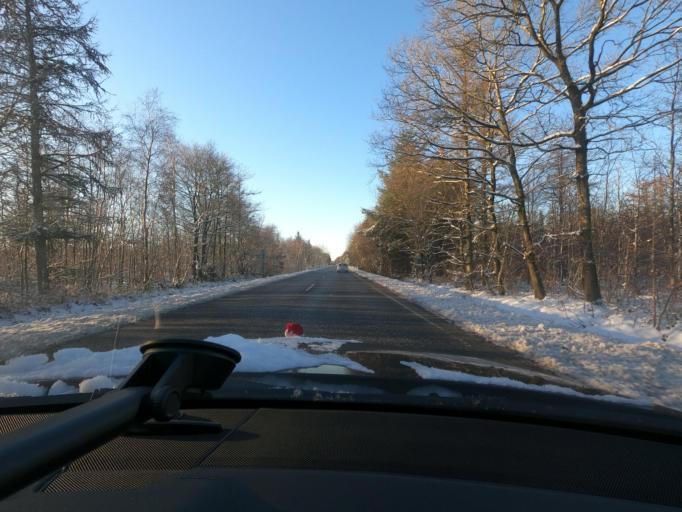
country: DK
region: South Denmark
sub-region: Tonder Kommune
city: Sherrebek
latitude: 55.1716
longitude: 8.7801
